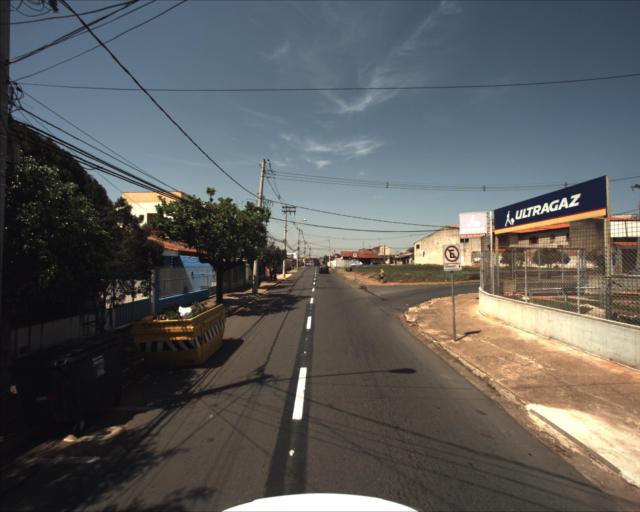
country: BR
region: Sao Paulo
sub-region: Sorocaba
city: Sorocaba
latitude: -23.4612
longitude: -47.4931
